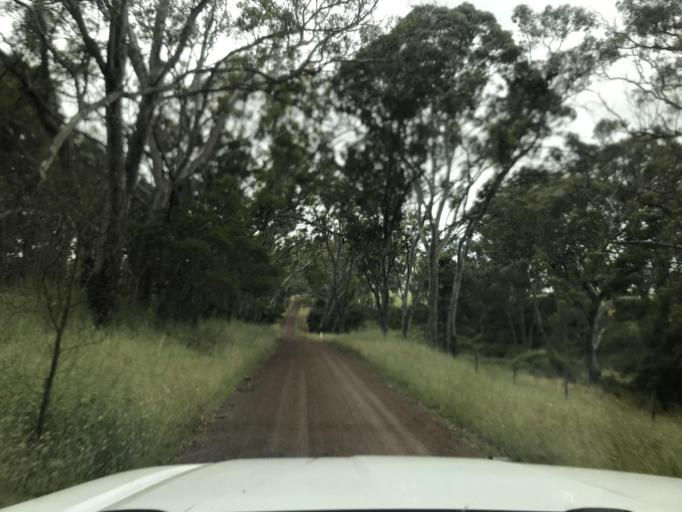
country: AU
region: South Australia
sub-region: Wattle Range
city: Penola
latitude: -37.2345
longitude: 141.4483
